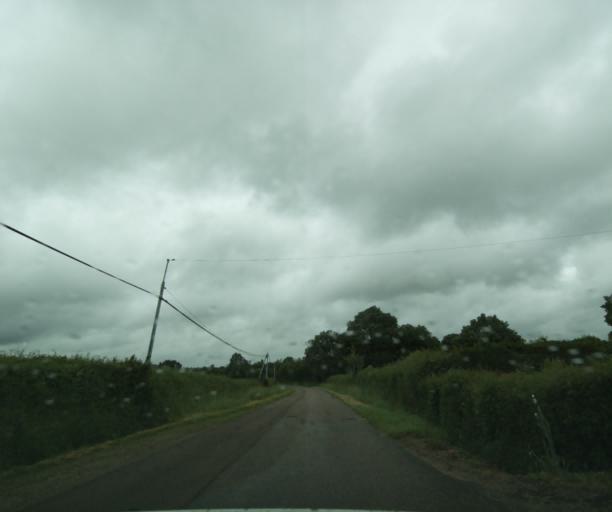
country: FR
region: Bourgogne
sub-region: Departement de Saone-et-Loire
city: Charolles
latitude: 46.4629
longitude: 4.4378
